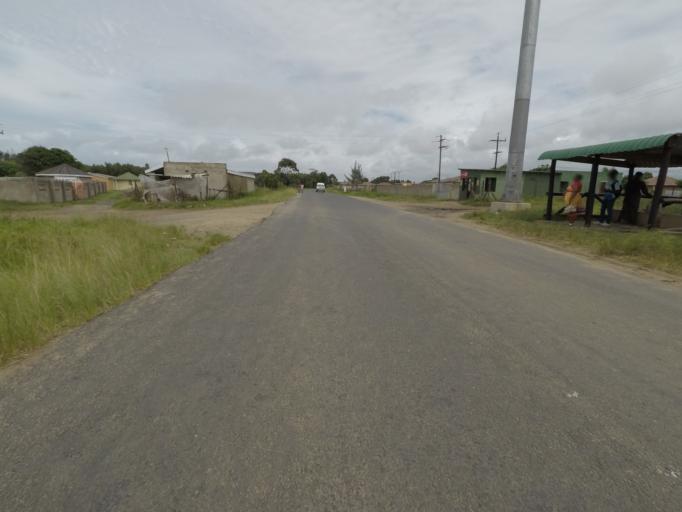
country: ZA
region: KwaZulu-Natal
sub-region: uThungulu District Municipality
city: eSikhawini
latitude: -28.9113
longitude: 31.8644
